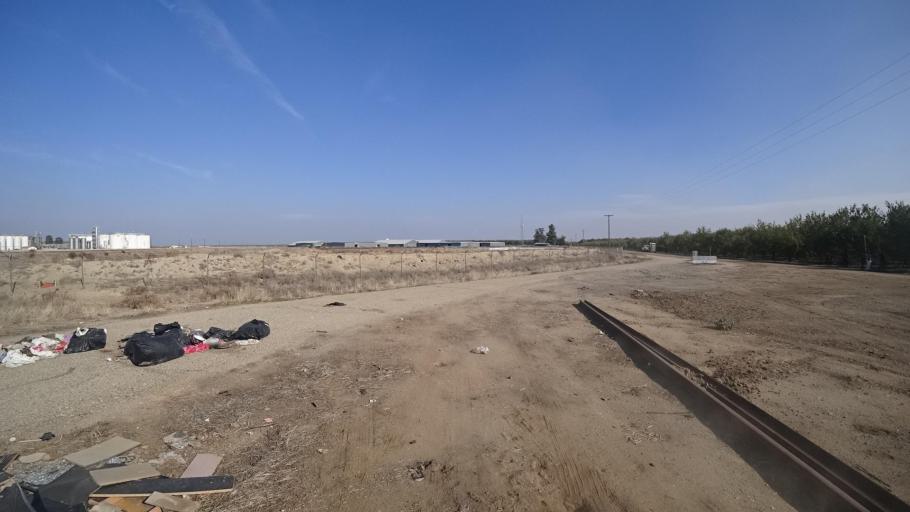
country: US
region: California
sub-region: Kern County
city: McFarland
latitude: 35.6313
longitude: -119.2135
